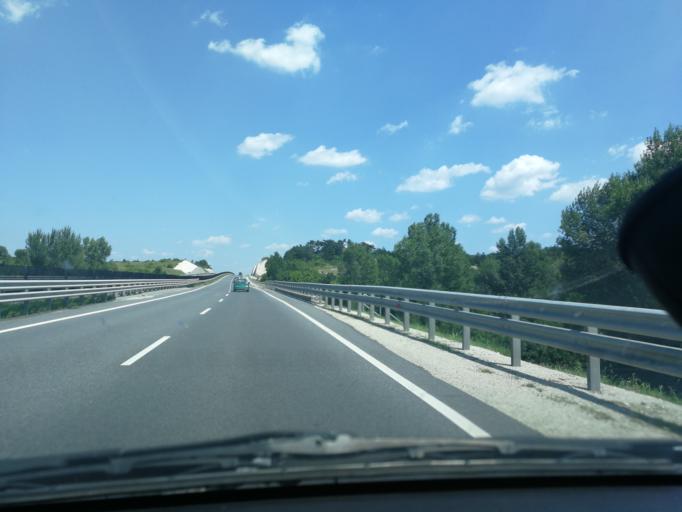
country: HU
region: Veszprem
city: Hajmasker
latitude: 47.1378
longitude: 18.0303
